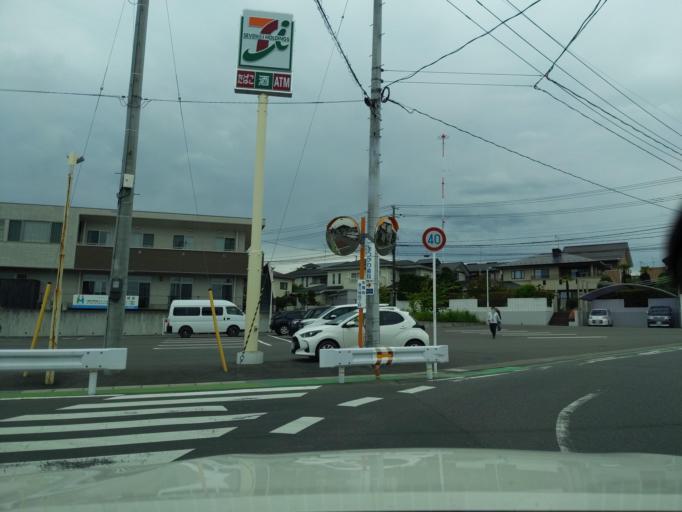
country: JP
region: Fukushima
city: Koriyama
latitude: 37.3581
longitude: 140.3583
